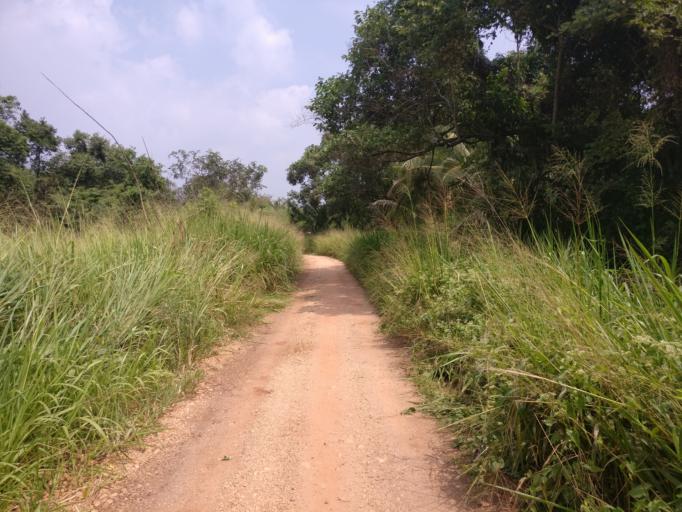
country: LK
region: Central
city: Dambulla
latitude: 7.8375
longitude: 80.6522
